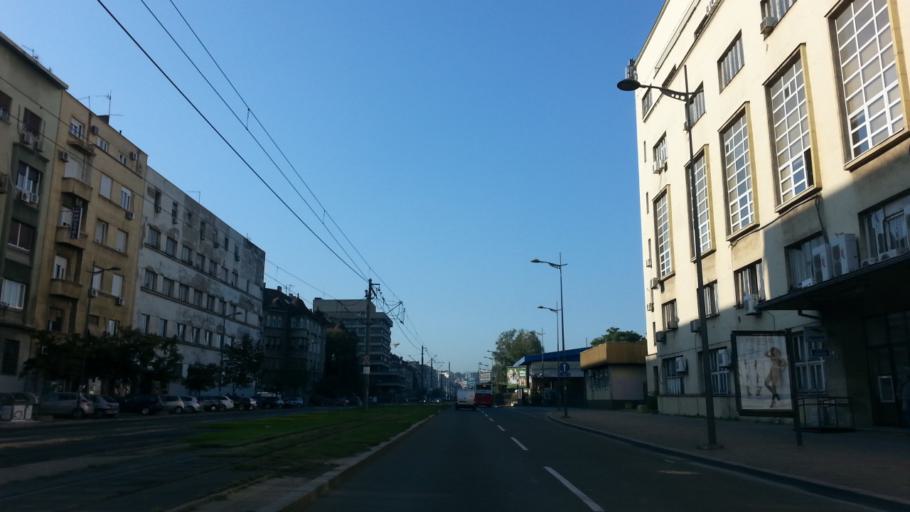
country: RS
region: Central Serbia
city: Belgrade
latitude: 44.8074
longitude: 20.4554
